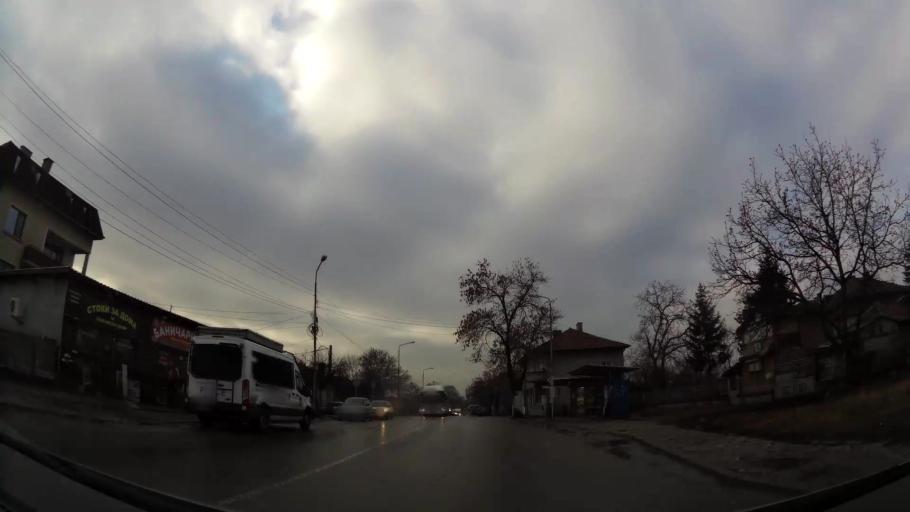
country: BG
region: Sofia-Capital
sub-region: Stolichna Obshtina
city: Sofia
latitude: 42.7375
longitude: 23.3435
